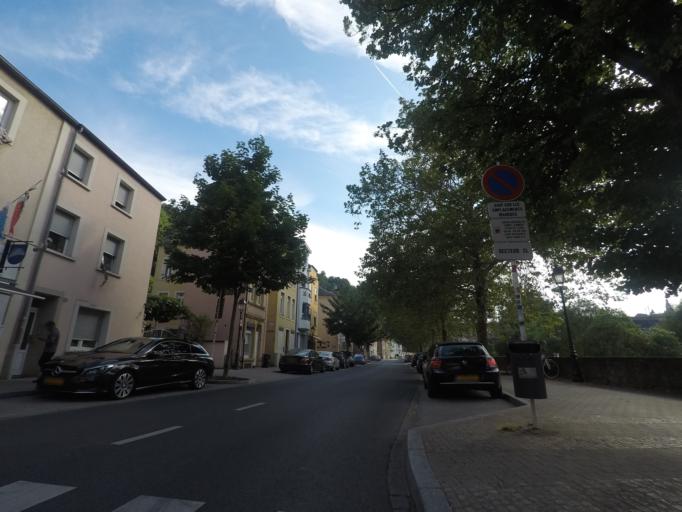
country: LU
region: Luxembourg
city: Kirchberg
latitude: 49.6129
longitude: 6.1440
